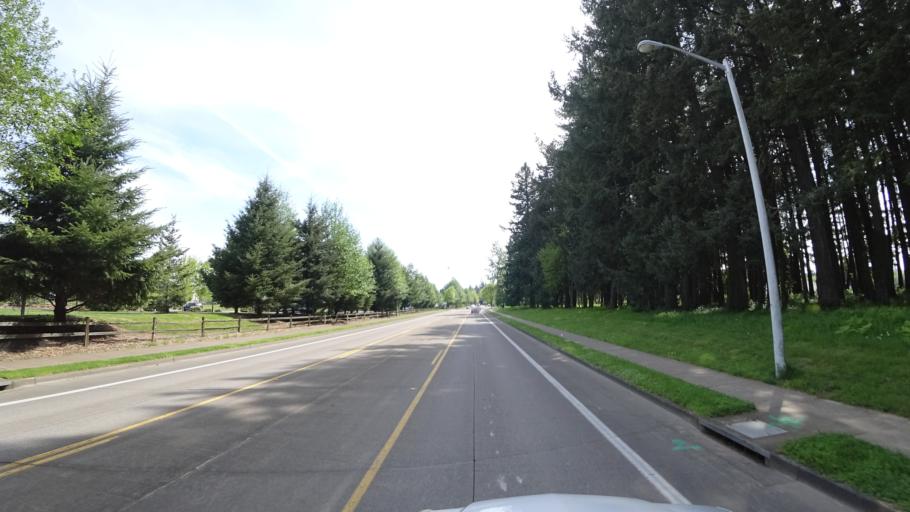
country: US
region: Oregon
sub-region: Washington County
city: Rockcreek
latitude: 45.5237
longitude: -122.9289
